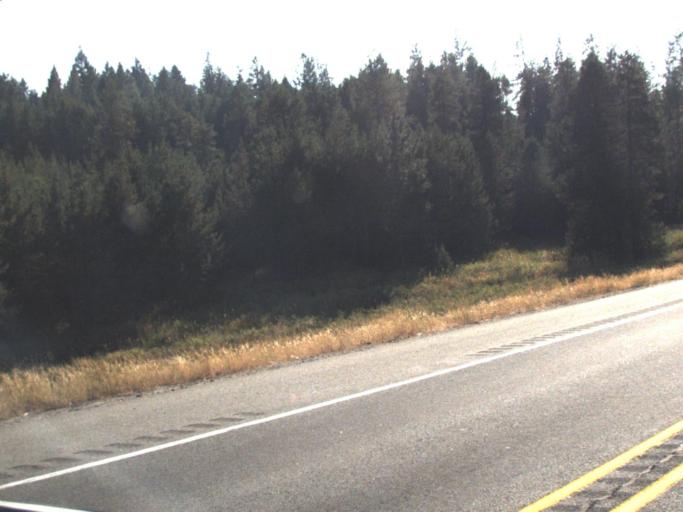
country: US
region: Washington
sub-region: Pend Oreille County
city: Newport
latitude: 48.1478
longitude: -117.1318
